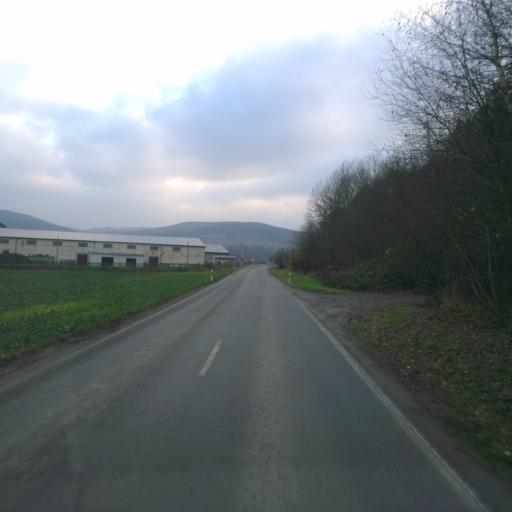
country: DE
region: Thuringia
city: Schops
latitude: 50.8348
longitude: 11.5880
